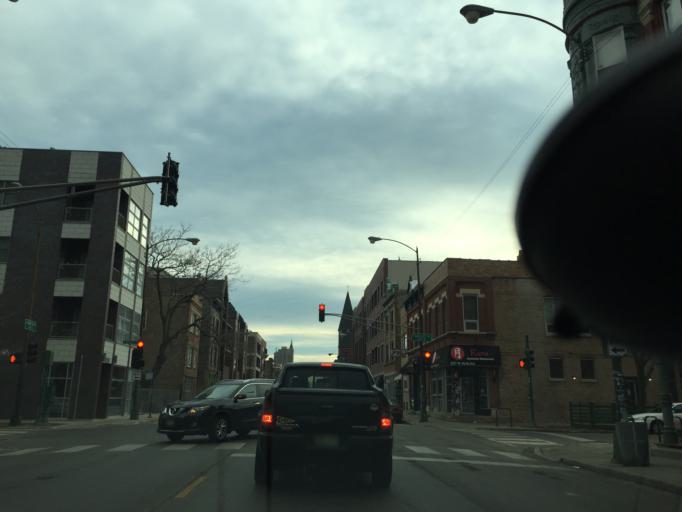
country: US
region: Illinois
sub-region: Cook County
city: Chicago
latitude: 41.9104
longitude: -87.6852
